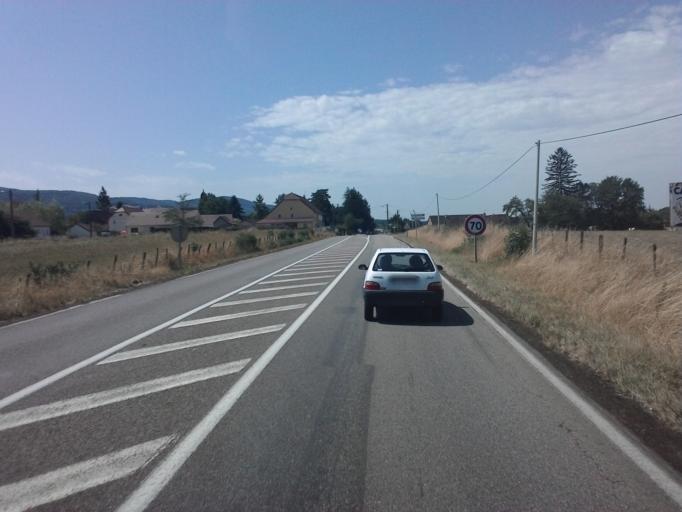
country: FR
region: Franche-Comte
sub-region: Departement du Jura
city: Montmorot
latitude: 46.6114
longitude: 5.4751
